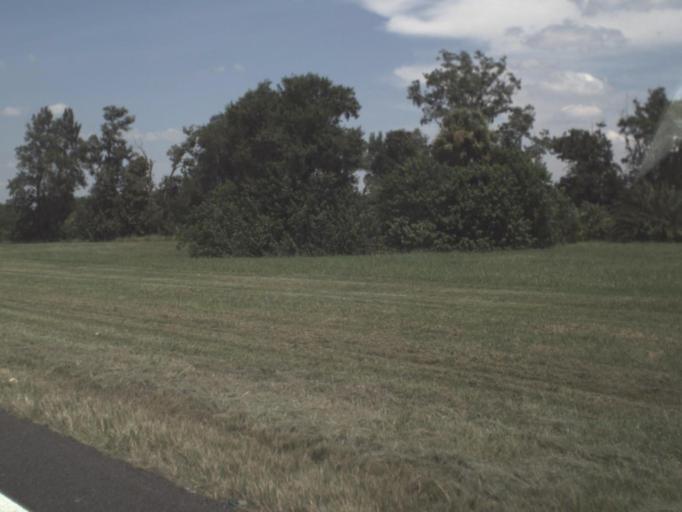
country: US
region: Florida
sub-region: Hillsborough County
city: Apollo Beach
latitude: 27.7548
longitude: -82.4059
